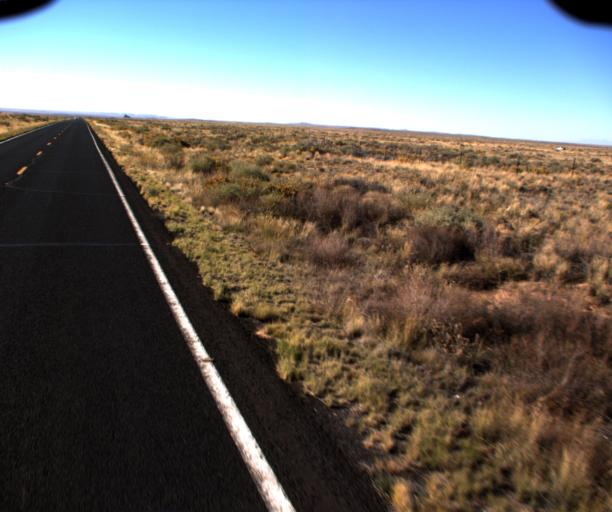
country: US
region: Arizona
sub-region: Navajo County
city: First Mesa
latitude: 35.7695
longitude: -110.5067
